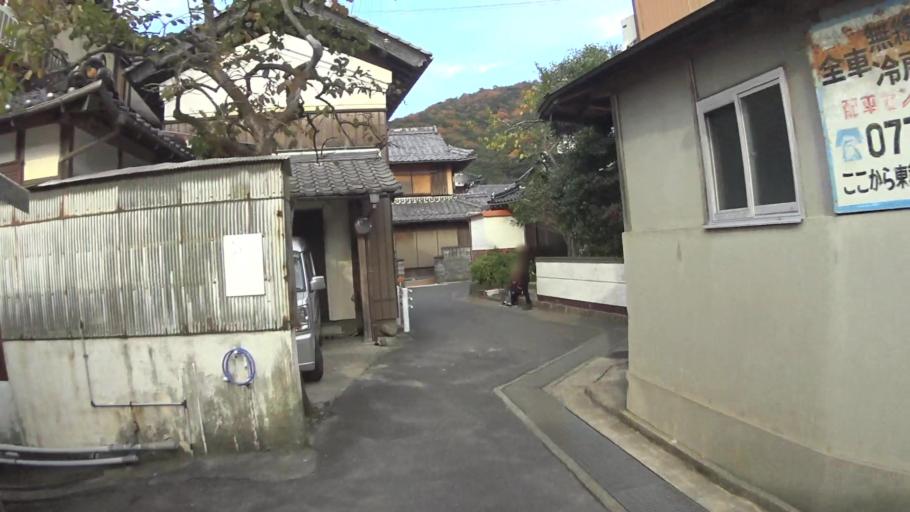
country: JP
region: Kyoto
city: Maizuru
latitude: 35.5687
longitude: 135.4284
